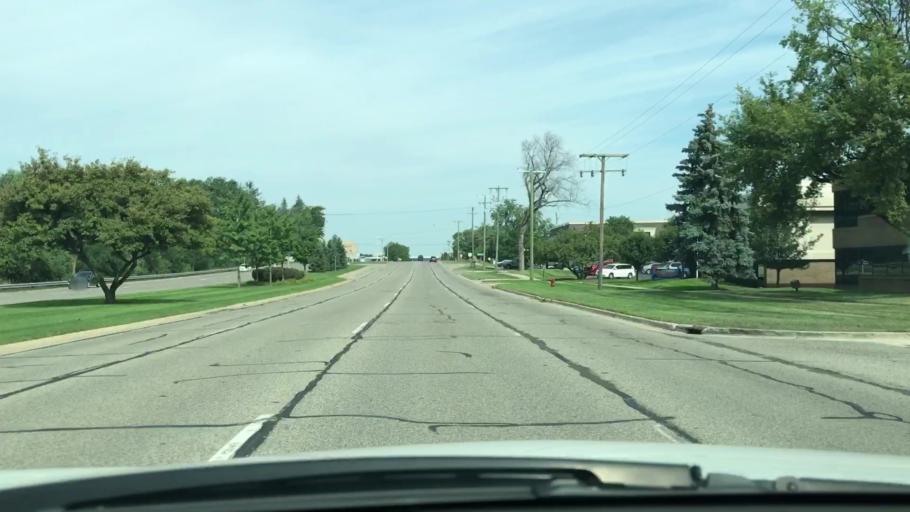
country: US
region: Michigan
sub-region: Oakland County
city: Pontiac
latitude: 42.6106
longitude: -83.2706
